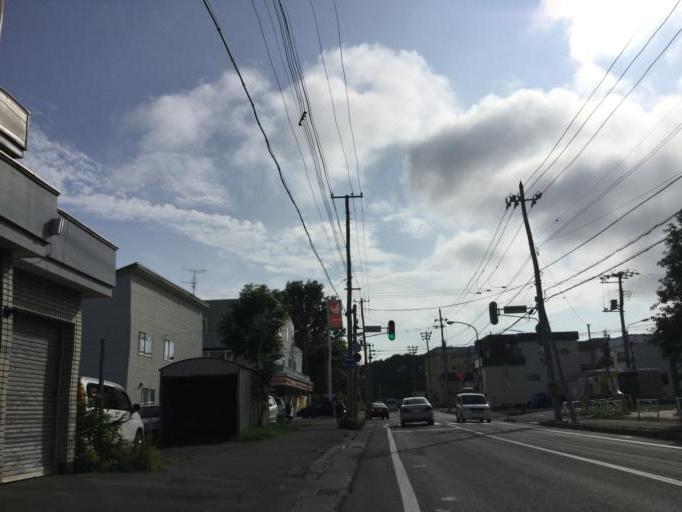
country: JP
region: Hokkaido
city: Wakkanai
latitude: 45.3943
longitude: 141.6852
